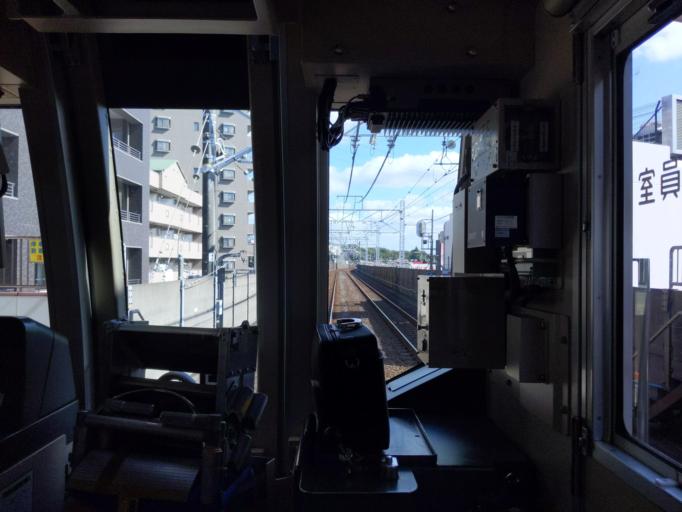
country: JP
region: Chiba
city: Yotsukaido
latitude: 35.7232
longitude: 140.1197
